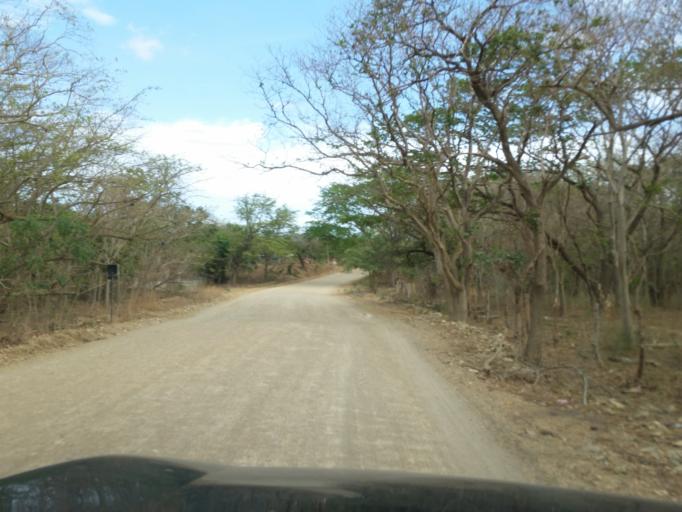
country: NI
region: Rivas
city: Tola
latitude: 11.4217
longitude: -86.0099
